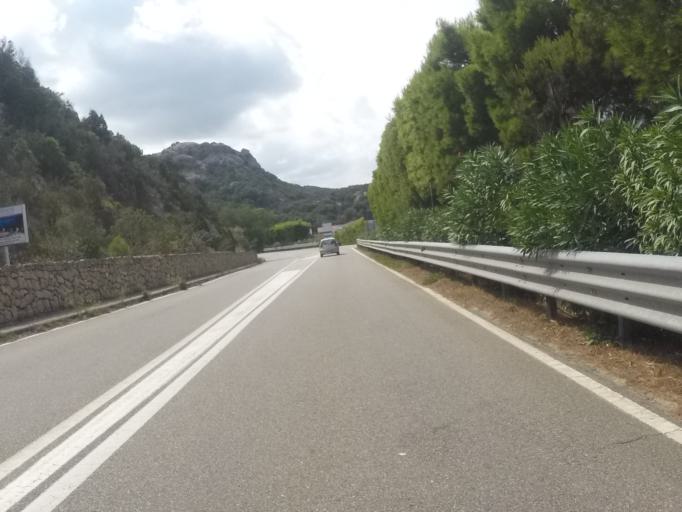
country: IT
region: Sardinia
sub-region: Provincia di Olbia-Tempio
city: Porto Cervo
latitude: 41.1358
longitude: 9.4995
